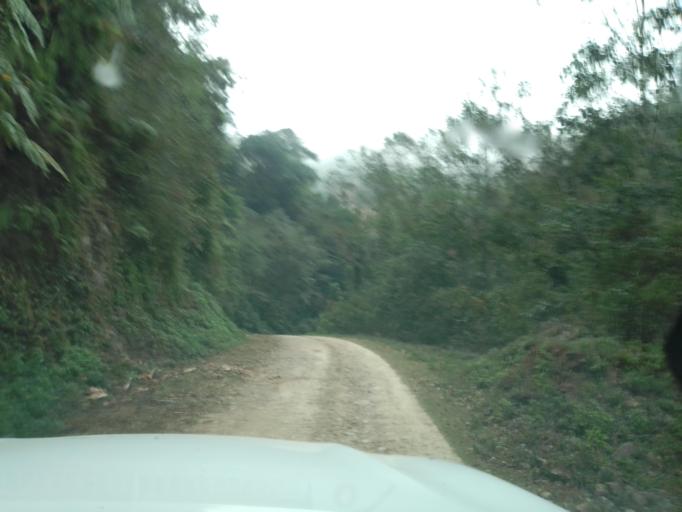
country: MX
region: Chiapas
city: Motozintla de Mendoza
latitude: 15.2174
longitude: -92.2218
